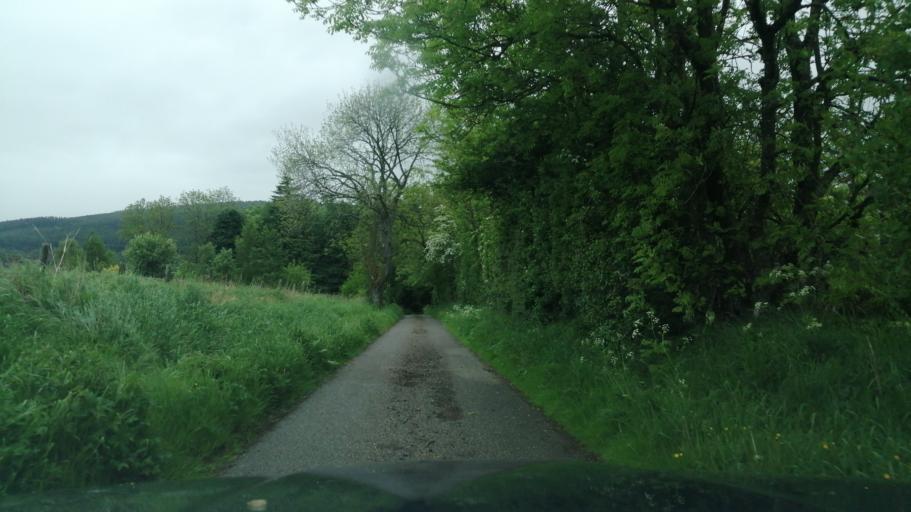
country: GB
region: Scotland
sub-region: Moray
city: Keith
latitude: 57.5526
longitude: -2.8711
